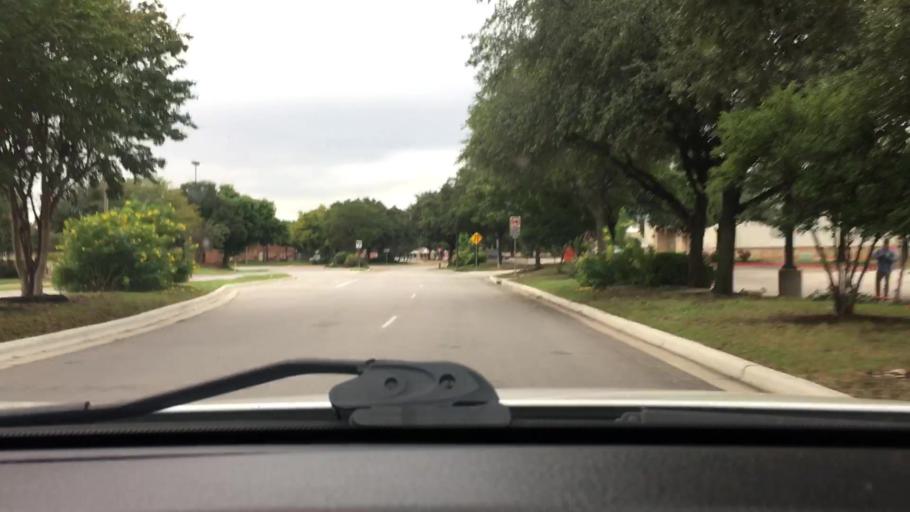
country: US
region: Texas
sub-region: Williamson County
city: Round Rock
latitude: 30.4819
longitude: -97.6806
